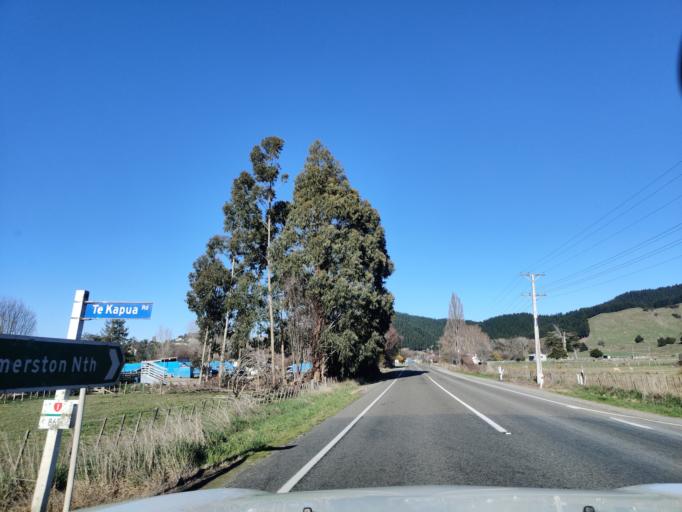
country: NZ
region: Manawatu-Wanganui
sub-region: Ruapehu District
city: Waiouru
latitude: -39.8133
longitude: 175.7842
